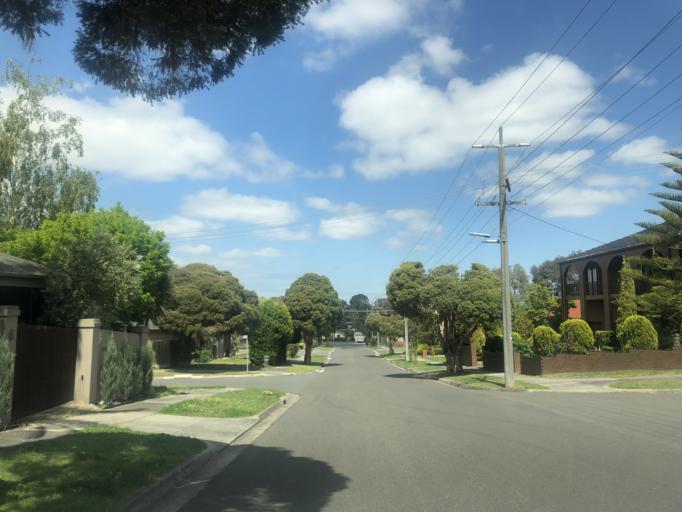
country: AU
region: Victoria
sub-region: Monash
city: Mulgrave
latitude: -37.9084
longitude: 145.1853
